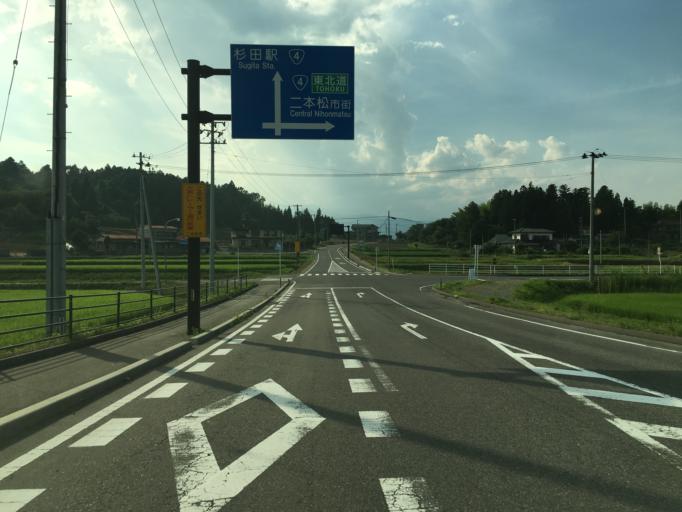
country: JP
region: Fukushima
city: Nihommatsu
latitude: 37.5547
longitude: 140.4341
